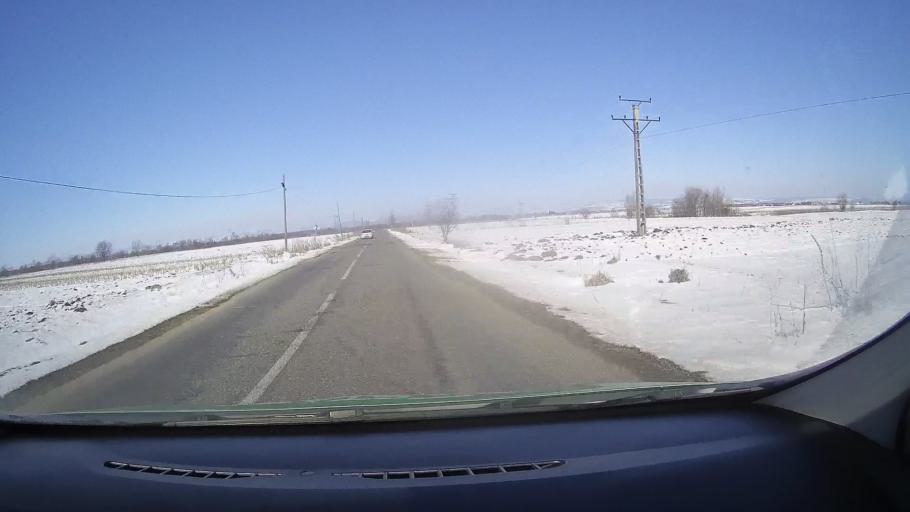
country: RO
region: Brasov
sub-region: Comuna Harseni
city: Harseni
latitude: 45.7683
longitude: 25.0036
